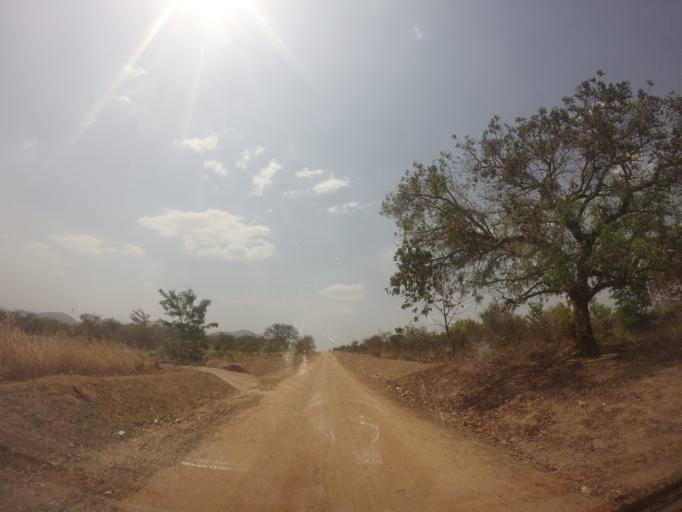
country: UG
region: Northern Region
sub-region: Arua District
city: Arua
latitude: 2.8970
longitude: 31.1275
